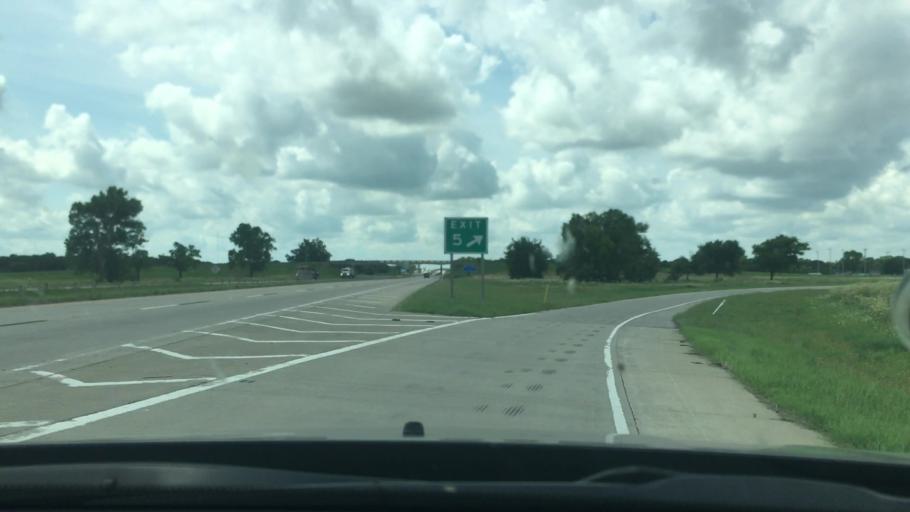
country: US
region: Oklahoma
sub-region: Love County
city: Marietta
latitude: 33.7985
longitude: -97.1351
